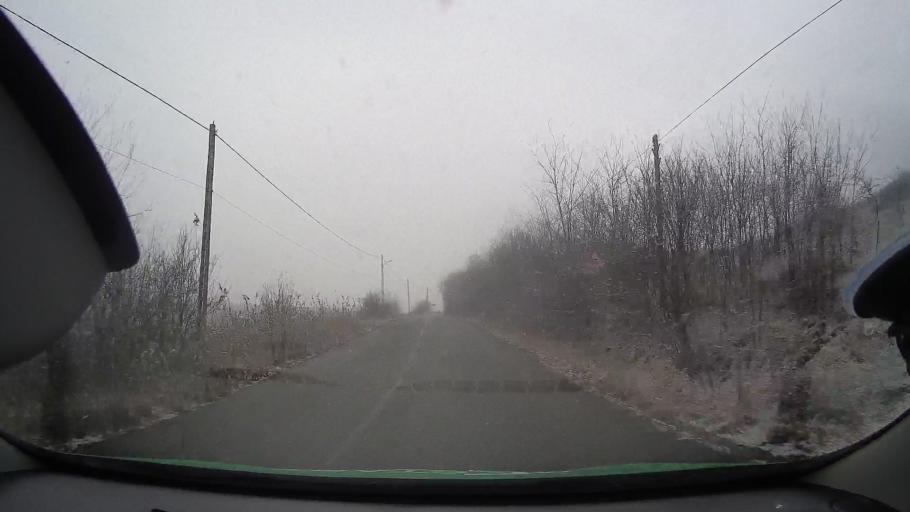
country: RO
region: Alba
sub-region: Comuna Noslac
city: Noslac
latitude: 46.3558
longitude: 23.9319
